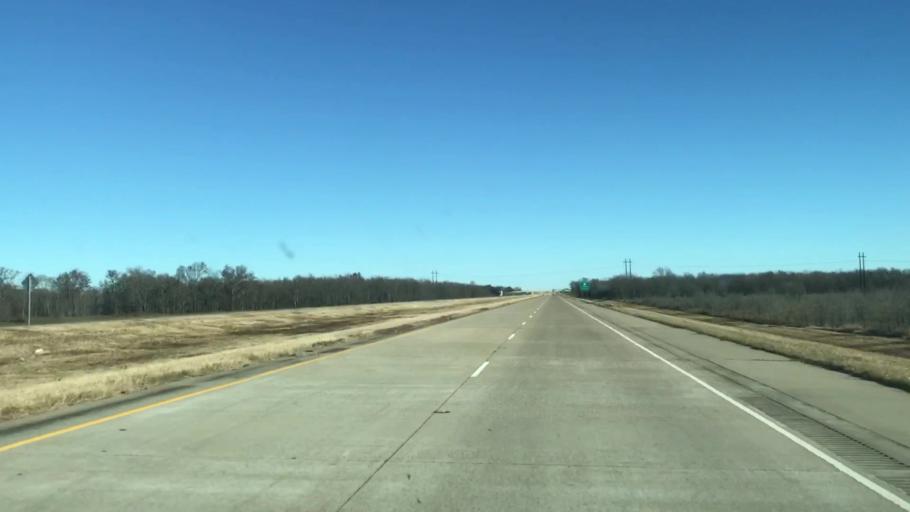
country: US
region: Louisiana
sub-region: Caddo Parish
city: Vivian
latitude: 32.8305
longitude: -93.8749
